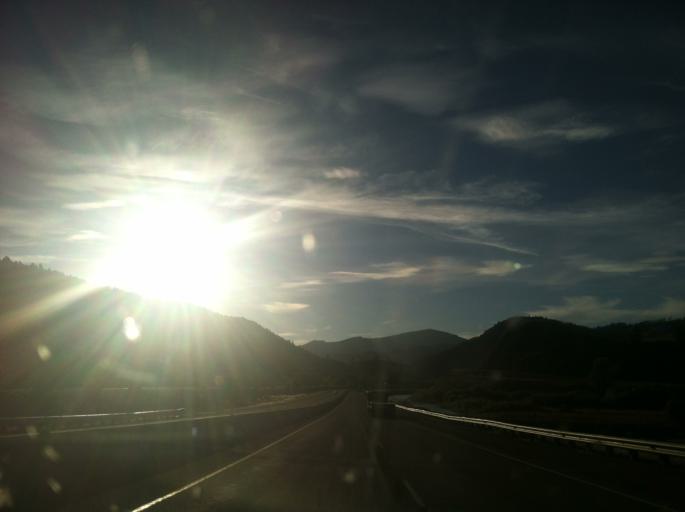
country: US
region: Montana
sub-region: Granite County
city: Philipsburg
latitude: 46.7131
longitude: -113.2732
